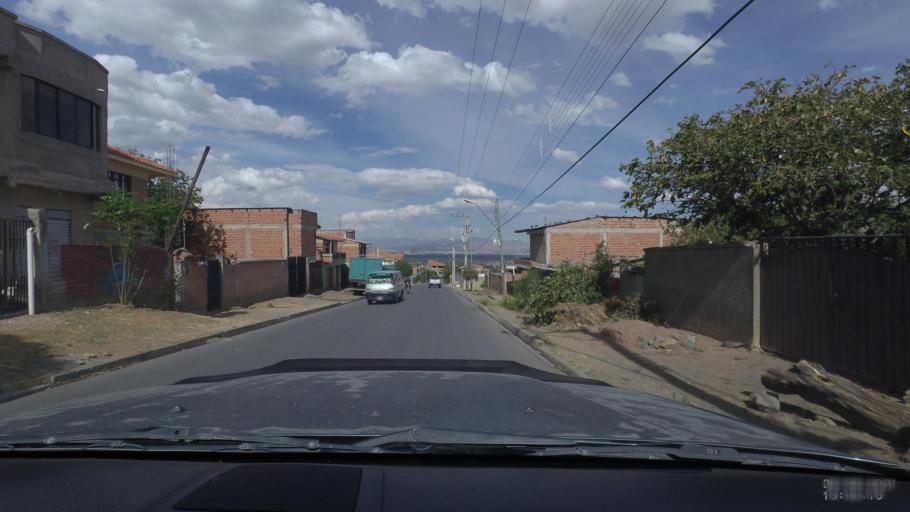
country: BO
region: Cochabamba
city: Cochabamba
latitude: -17.3137
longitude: -66.2866
